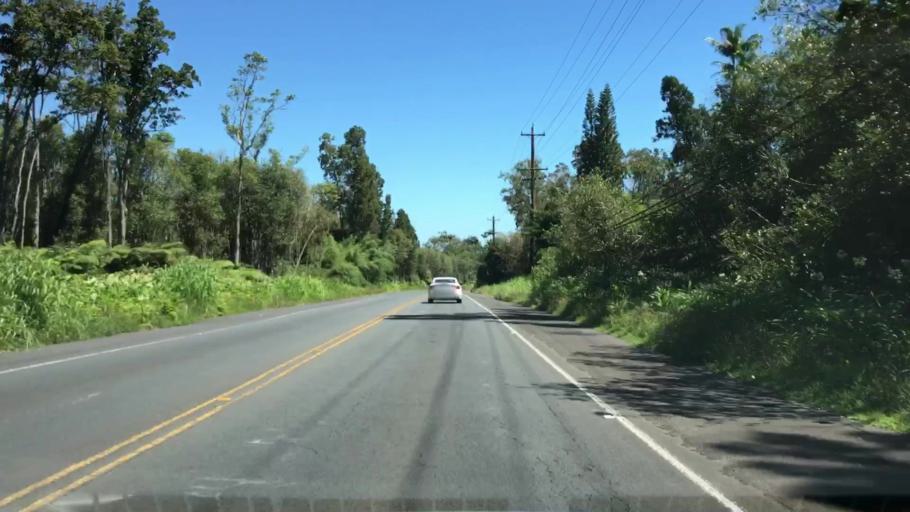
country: US
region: Hawaii
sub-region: Hawaii County
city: Mountain View
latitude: 19.5255
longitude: -155.1350
